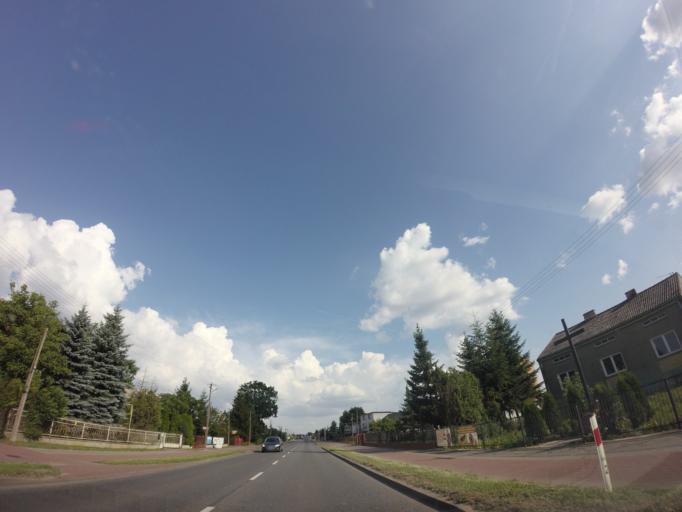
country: PL
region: Masovian Voivodeship
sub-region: Siedlce
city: Siedlce
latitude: 52.2033
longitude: 22.2478
